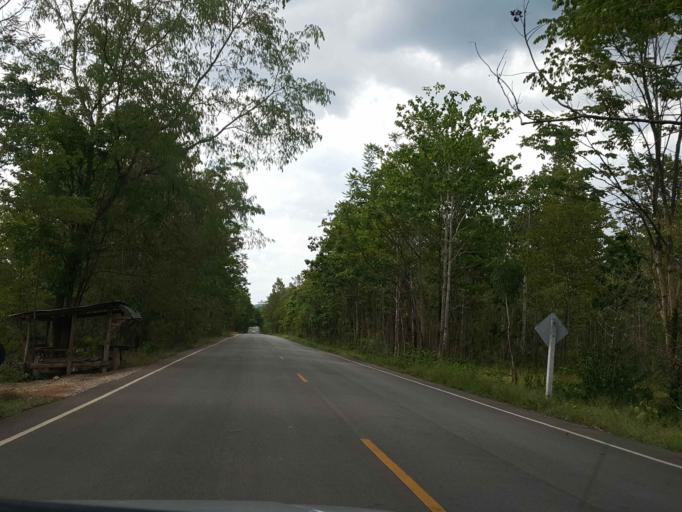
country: TH
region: Sukhothai
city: Thung Saliam
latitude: 17.3805
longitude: 99.4002
